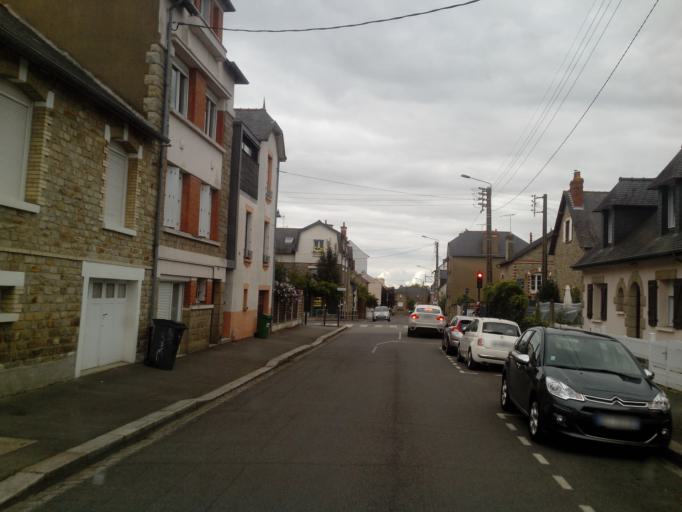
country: FR
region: Brittany
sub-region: Departement d'Ille-et-Vilaine
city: Rennes
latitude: 48.0976
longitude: -1.6669
